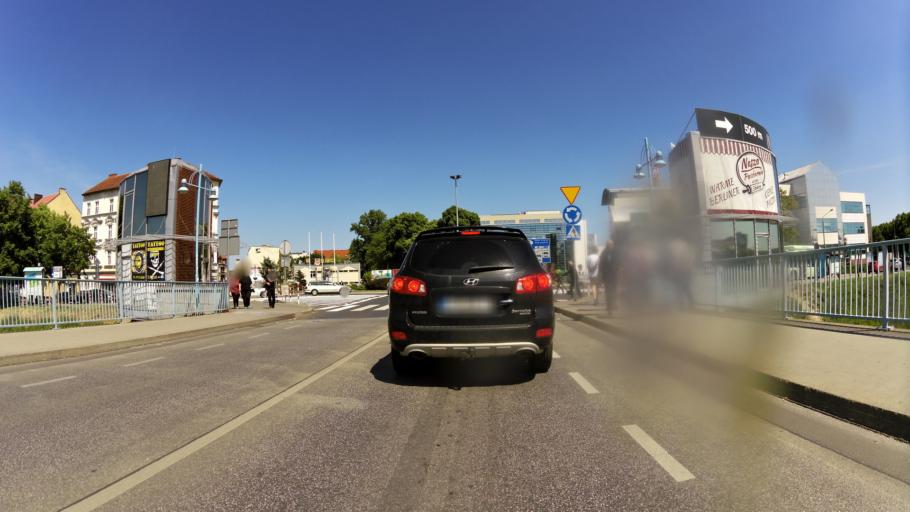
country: PL
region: Lubusz
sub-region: Powiat slubicki
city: Slubice
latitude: 52.3486
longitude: 14.5572
